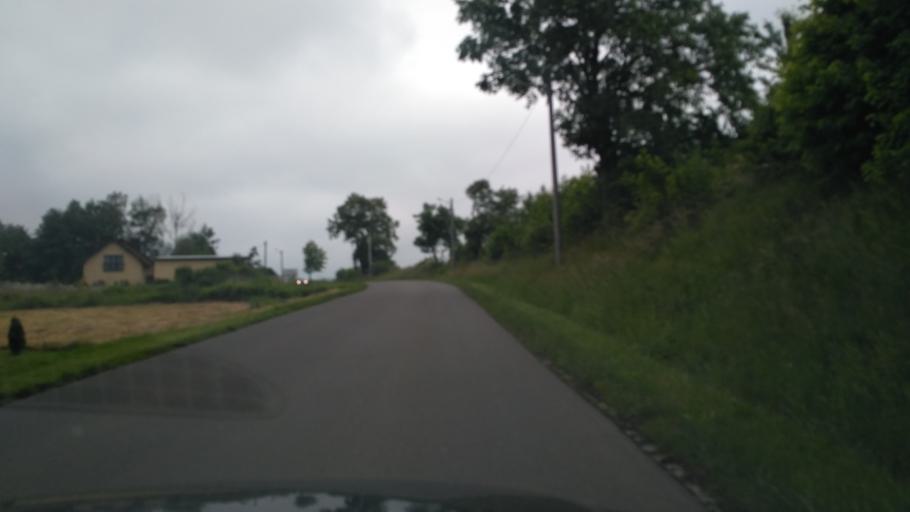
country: PL
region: Subcarpathian Voivodeship
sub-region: Powiat ropczycko-sedziszowski
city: Sedziszow Malopolski
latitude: 50.0473
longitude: 21.6968
